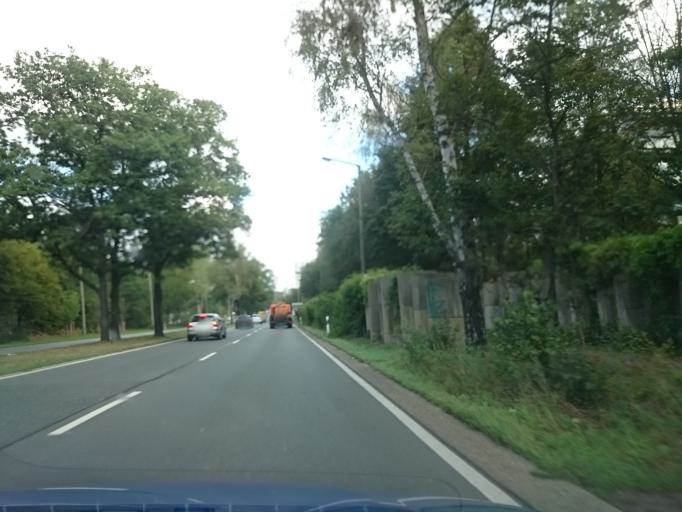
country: DE
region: Bavaria
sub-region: Regierungsbezirk Mittelfranken
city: Nuernberg
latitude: 49.4092
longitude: 11.1139
